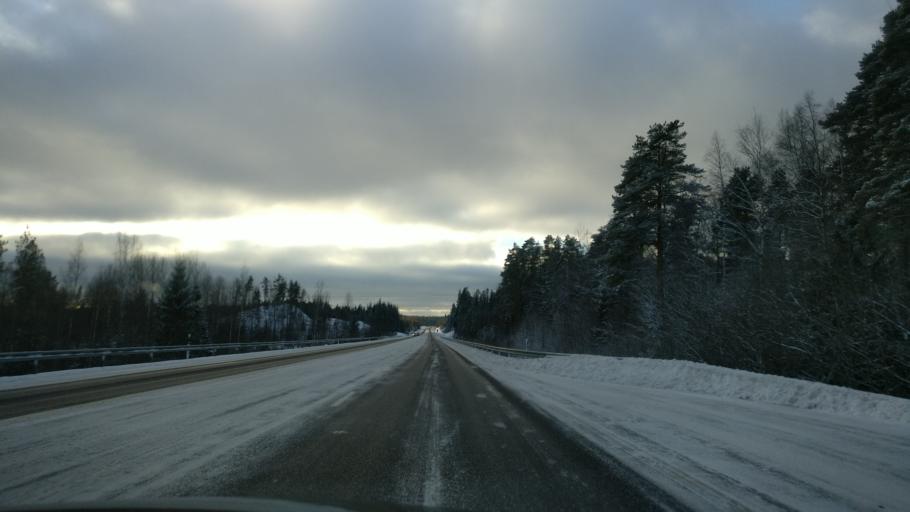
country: FI
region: Paijanne Tavastia
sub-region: Lahti
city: Heinola
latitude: 61.3595
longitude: 26.2370
